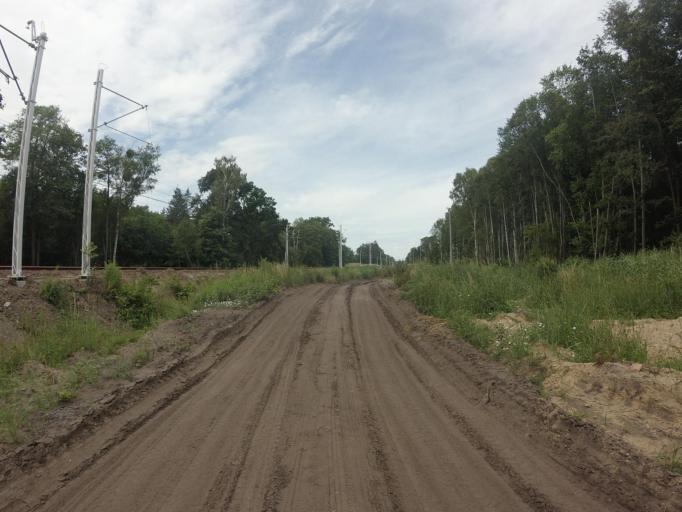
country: PL
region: West Pomeranian Voivodeship
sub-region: Powiat choszczenski
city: Bierzwnik
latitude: 53.0330
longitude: 15.6361
